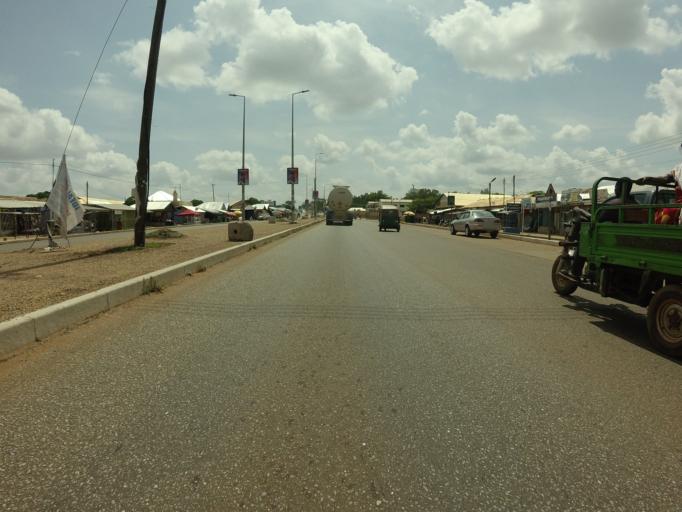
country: GH
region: Northern
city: Tamale
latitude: 9.3985
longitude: -0.8303
